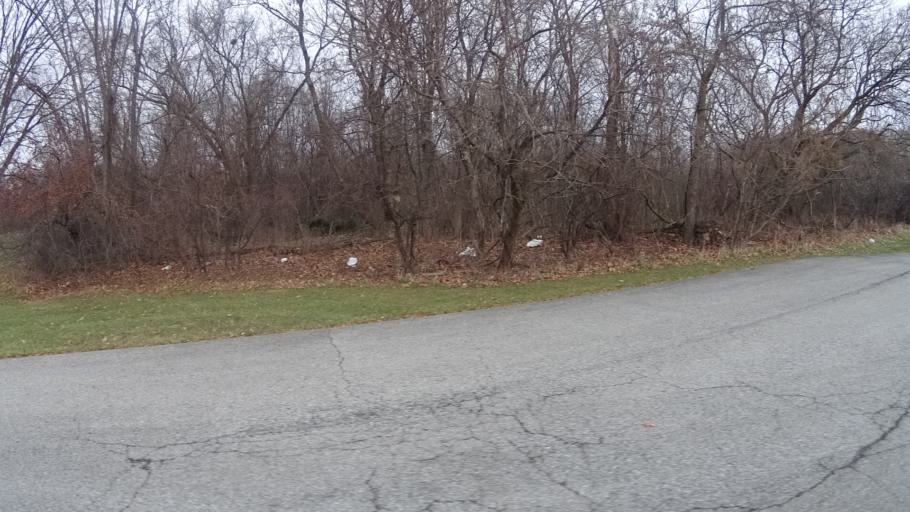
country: US
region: Ohio
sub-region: Lorain County
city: Wellington
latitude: 41.1656
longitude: -82.2082
